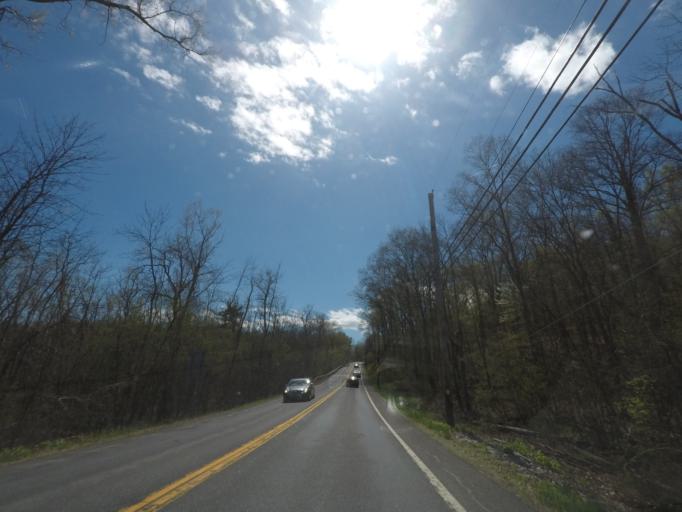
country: US
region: New York
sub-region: Greene County
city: Athens
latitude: 42.2488
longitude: -73.8407
